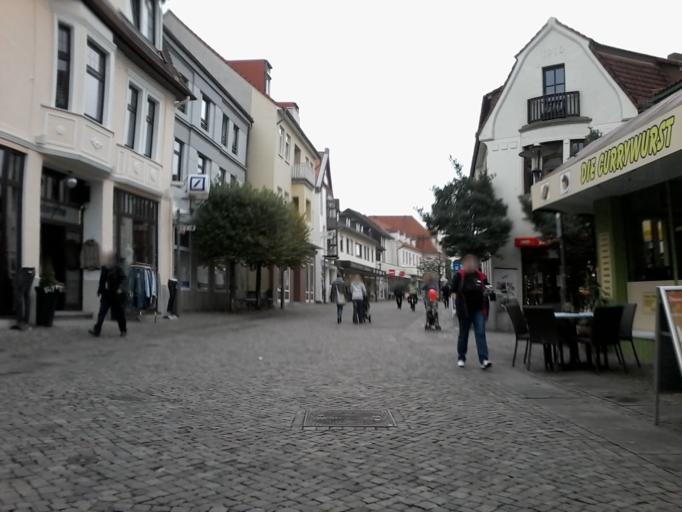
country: DE
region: Lower Saxony
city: Achim
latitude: 53.0129
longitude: 9.0340
